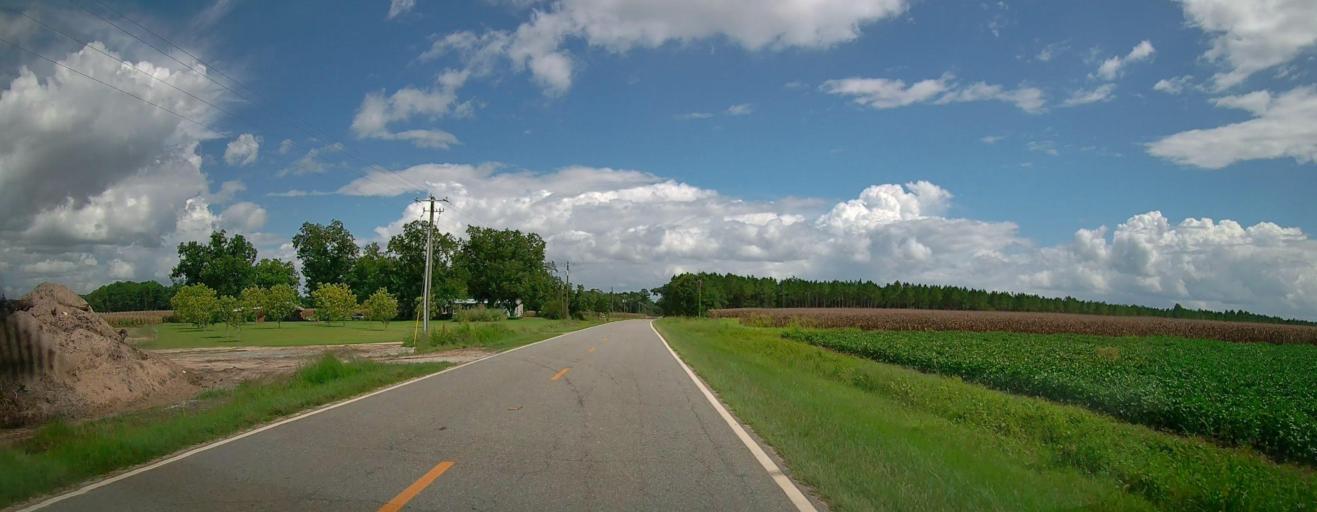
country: US
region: Georgia
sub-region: Ben Hill County
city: Fitzgerald
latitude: 31.6649
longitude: -83.1830
